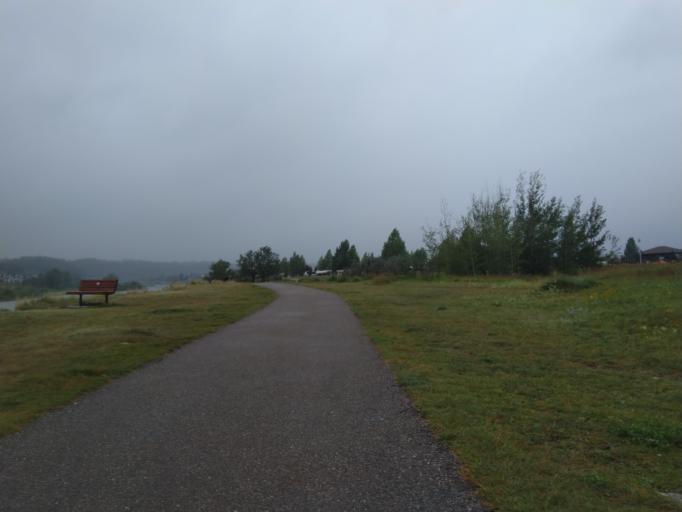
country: CA
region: Alberta
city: Cochrane
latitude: 51.1739
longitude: -114.4533
